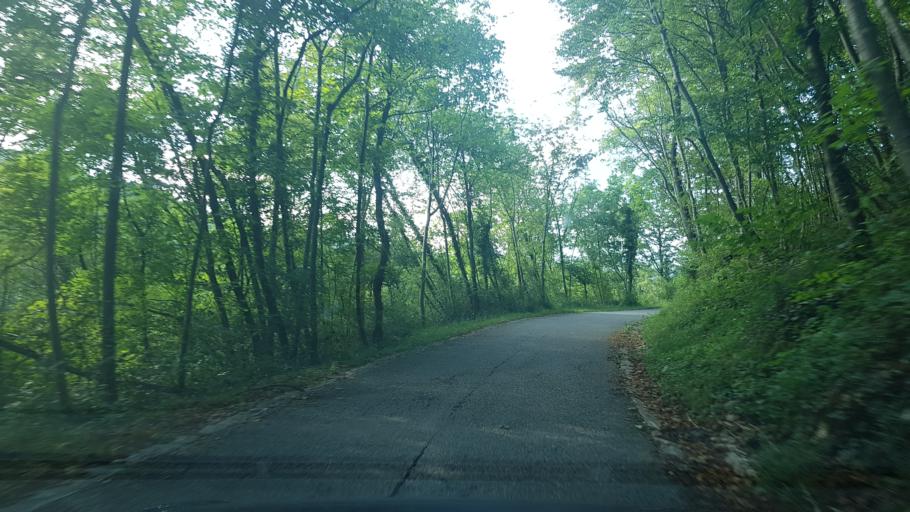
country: SI
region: Kanal
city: Deskle
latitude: 46.0291
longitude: 13.5998
